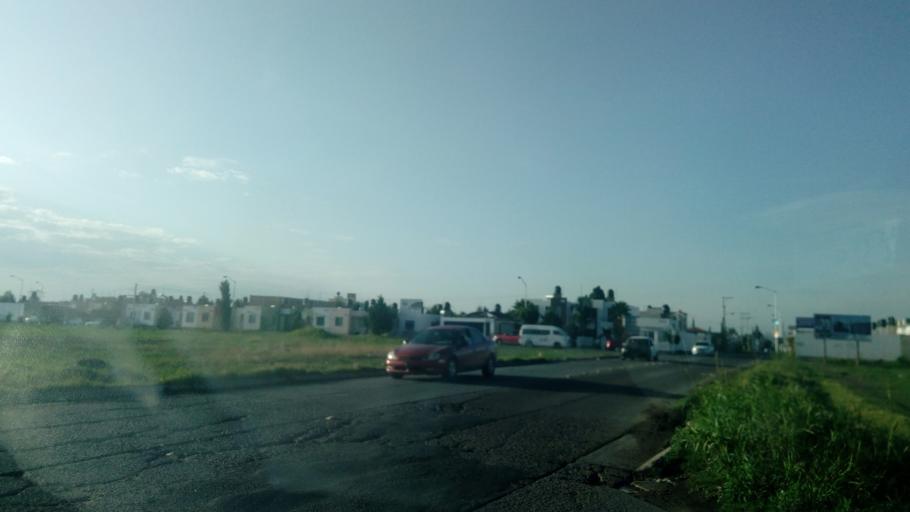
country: MX
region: Durango
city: Victoria de Durango
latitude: 24.0742
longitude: -104.5903
